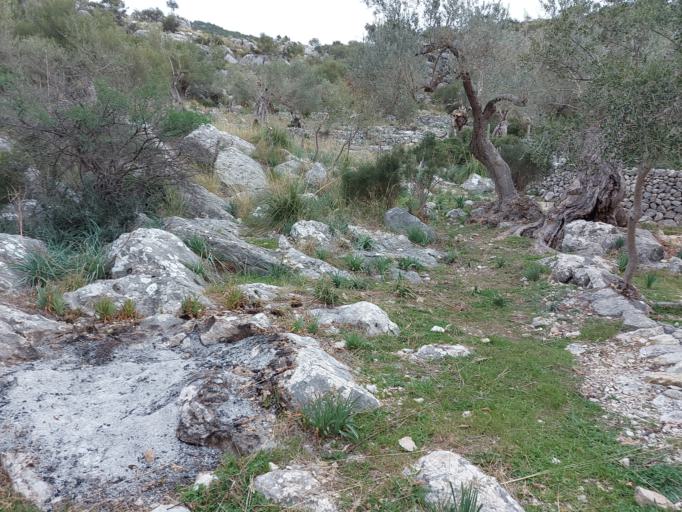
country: ES
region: Balearic Islands
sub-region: Illes Balears
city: Mancor de la Vall
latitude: 39.7688
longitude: 2.8190
